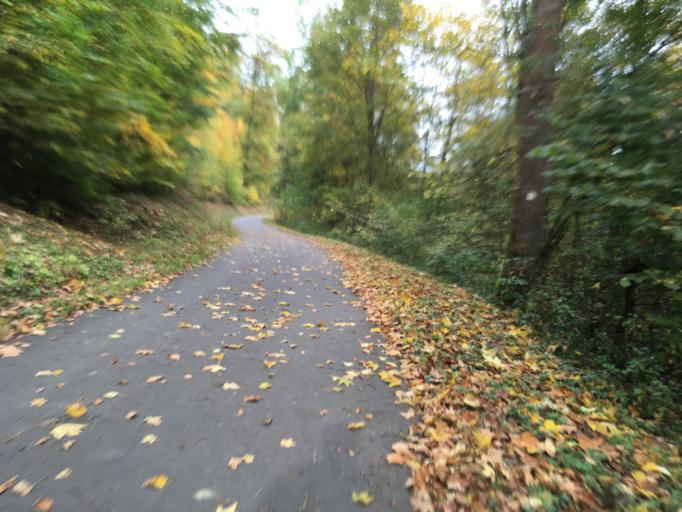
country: DE
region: Baden-Wuerttemberg
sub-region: Karlsruhe Region
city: Adelsheim
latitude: 49.4165
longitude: 9.3881
